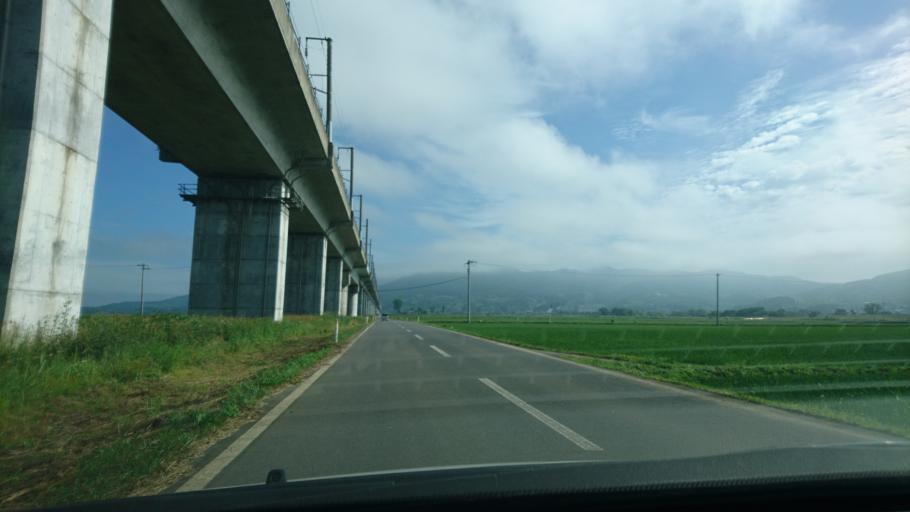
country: JP
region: Iwate
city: Ichinoseki
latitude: 38.9548
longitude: 141.1499
